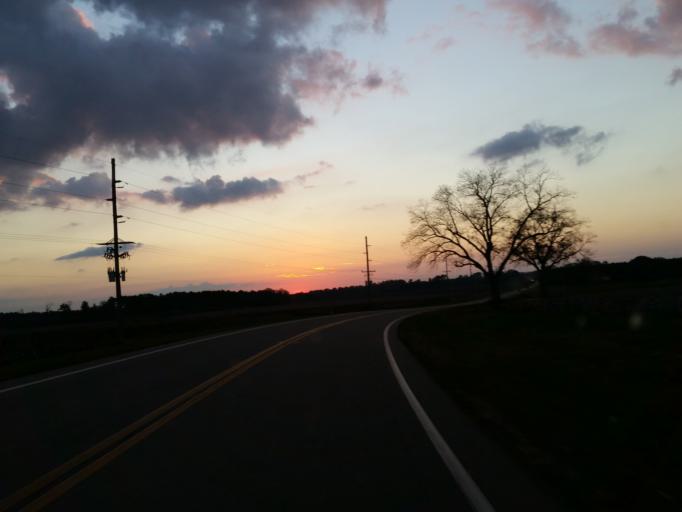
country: US
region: Georgia
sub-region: Dooly County
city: Vienna
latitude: 32.1237
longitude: -83.7170
